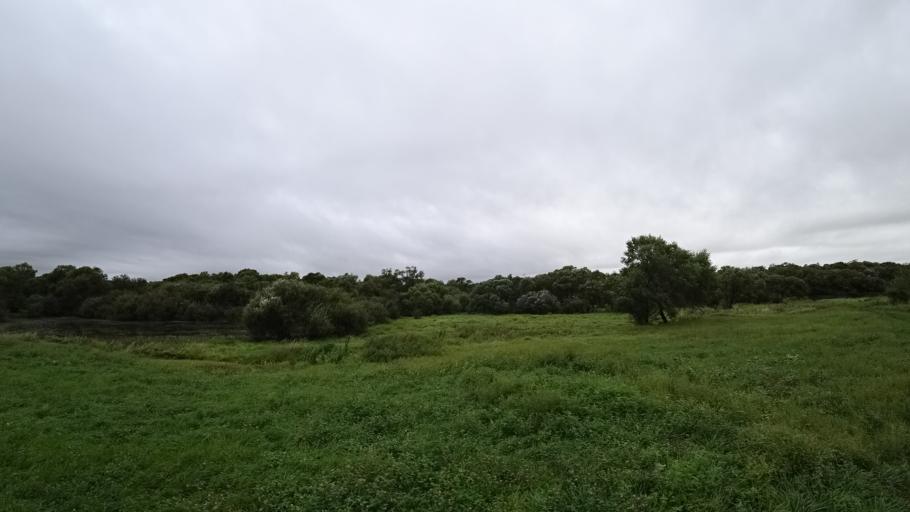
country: RU
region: Primorskiy
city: Monastyrishche
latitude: 44.2711
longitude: 132.4047
